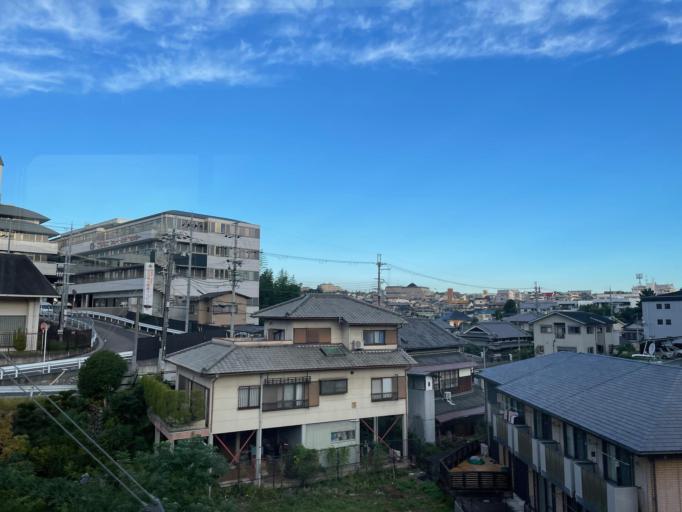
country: JP
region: Osaka
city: Tondabayashicho
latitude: 34.4488
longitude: 135.5717
